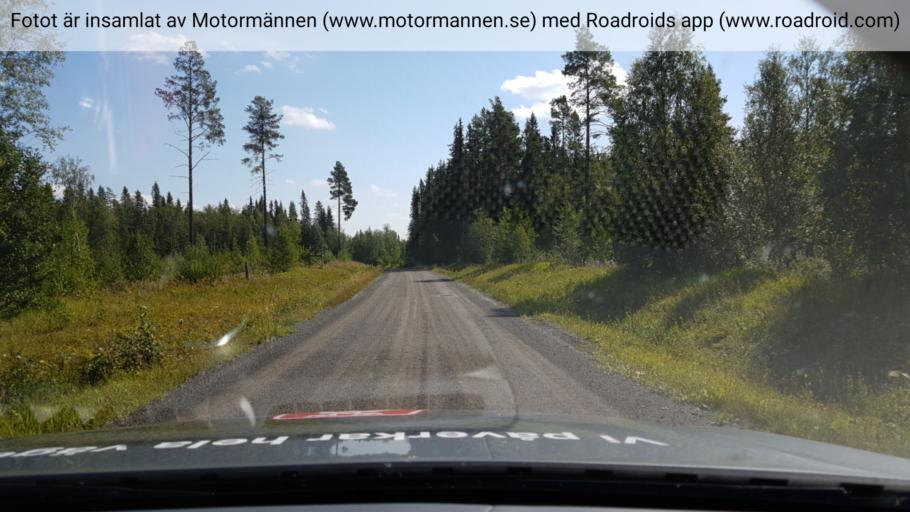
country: SE
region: Jaemtland
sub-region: OEstersunds Kommun
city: Lit
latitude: 63.3503
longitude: 15.2425
